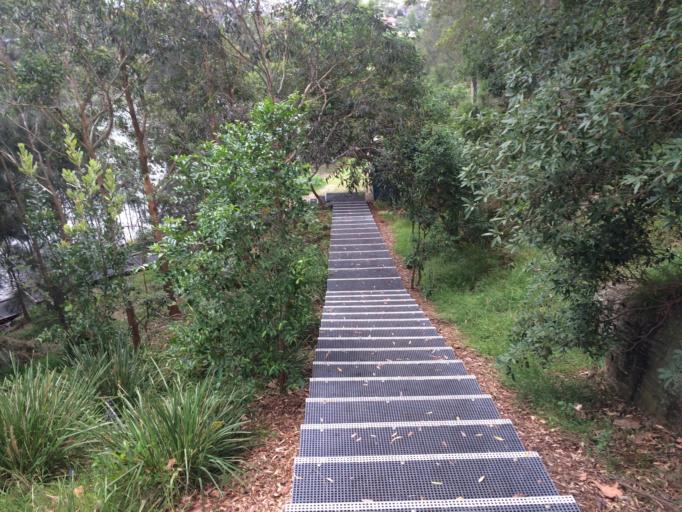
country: AU
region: New South Wales
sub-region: Hunters Hill
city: Gladesville
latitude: -33.8342
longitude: 151.1208
